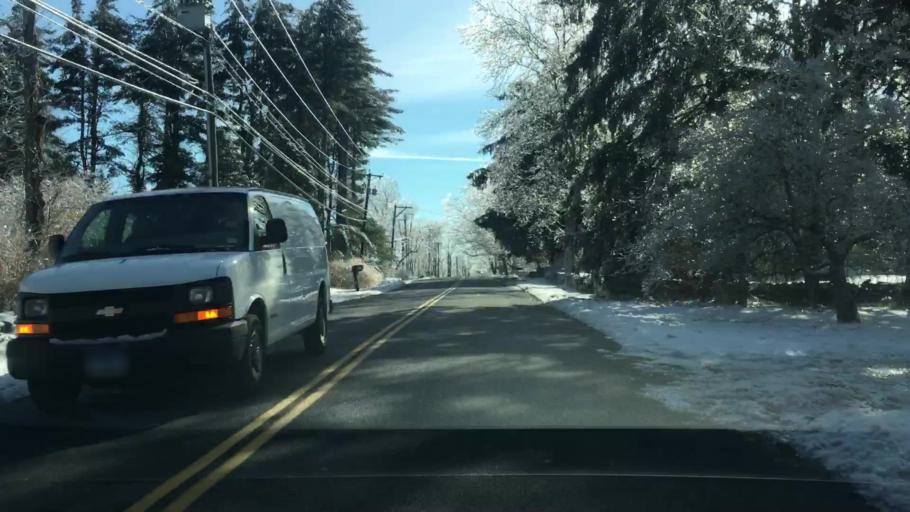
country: US
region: Connecticut
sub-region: Fairfield County
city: Trumbull
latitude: 41.3252
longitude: -73.2212
